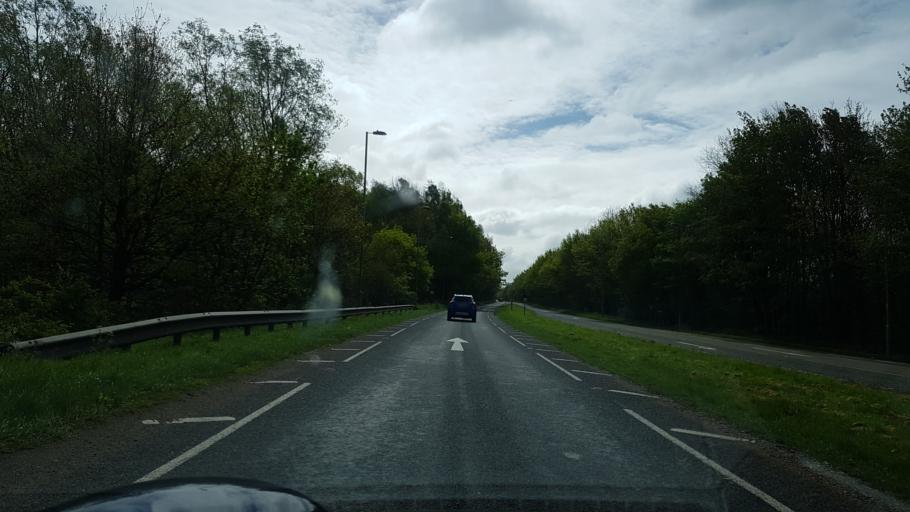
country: GB
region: England
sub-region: Hampshire
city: Kingsclere
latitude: 51.3276
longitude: -1.2386
